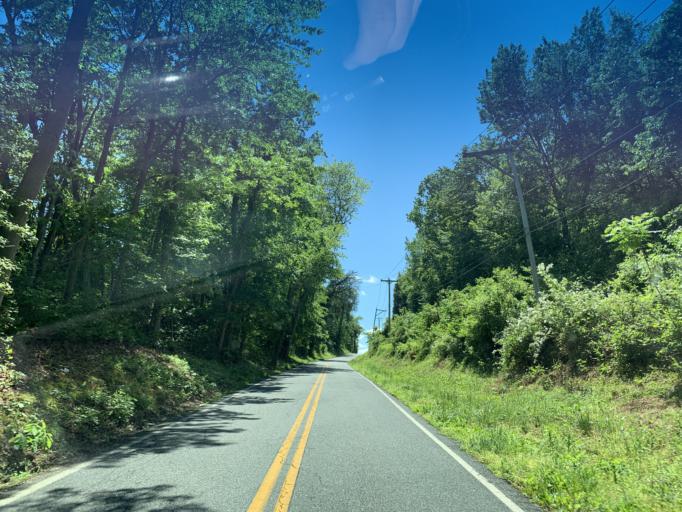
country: US
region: Maryland
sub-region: Cecil County
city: Charlestown
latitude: 39.5181
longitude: -75.9448
